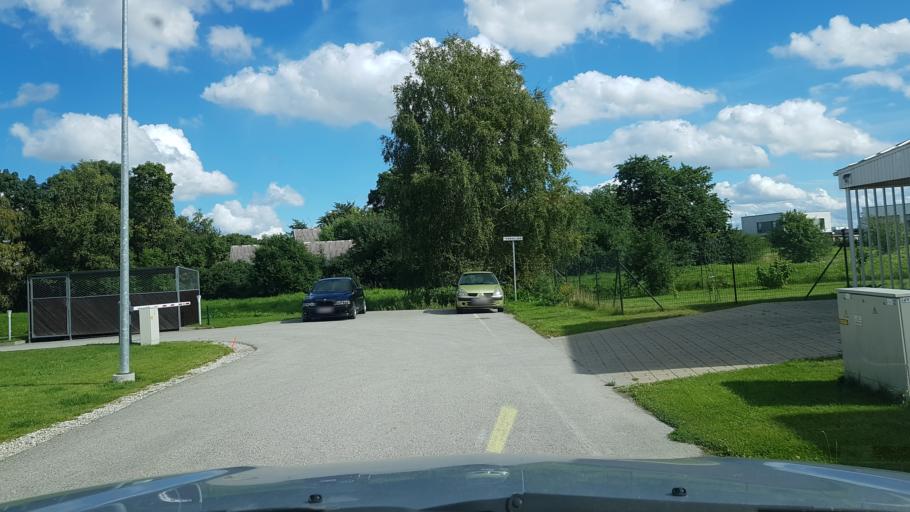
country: EE
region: Harju
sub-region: Tallinna linn
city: Tallinn
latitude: 59.3949
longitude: 24.7969
